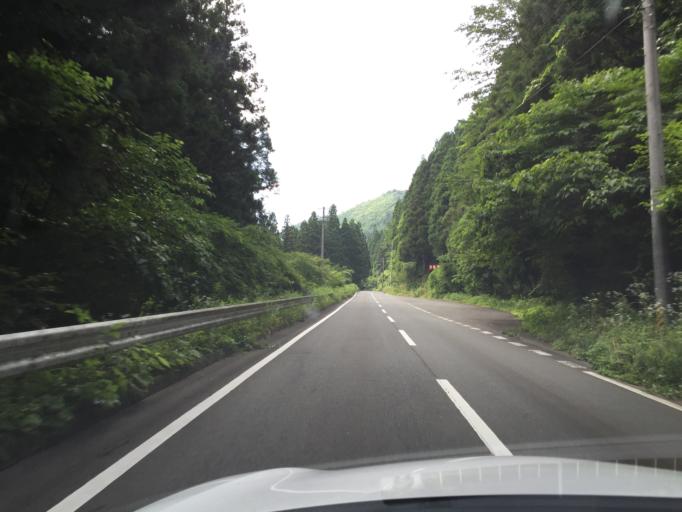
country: JP
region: Fukushima
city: Iwaki
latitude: 37.0716
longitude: 140.6886
